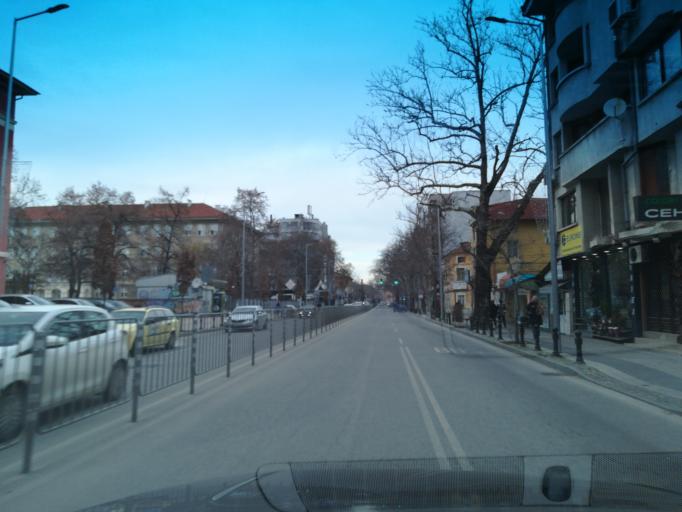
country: BG
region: Plovdiv
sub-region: Obshtina Plovdiv
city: Plovdiv
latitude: 42.1368
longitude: 24.7413
